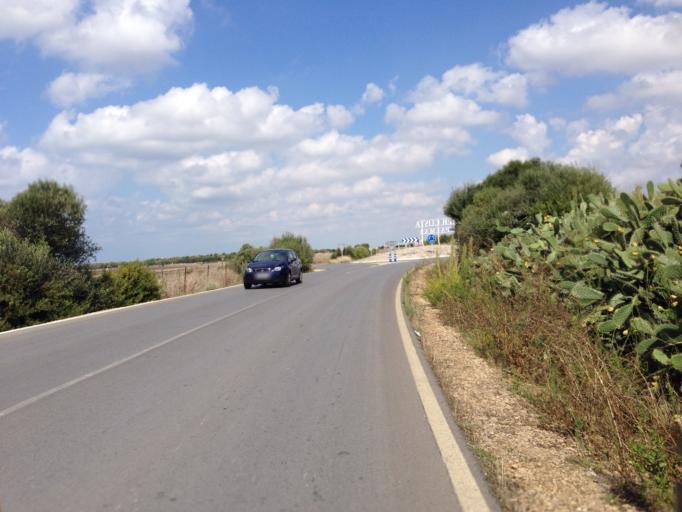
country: ES
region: Andalusia
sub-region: Provincia de Cadiz
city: Conil de la Frontera
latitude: 36.2204
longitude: -6.0407
